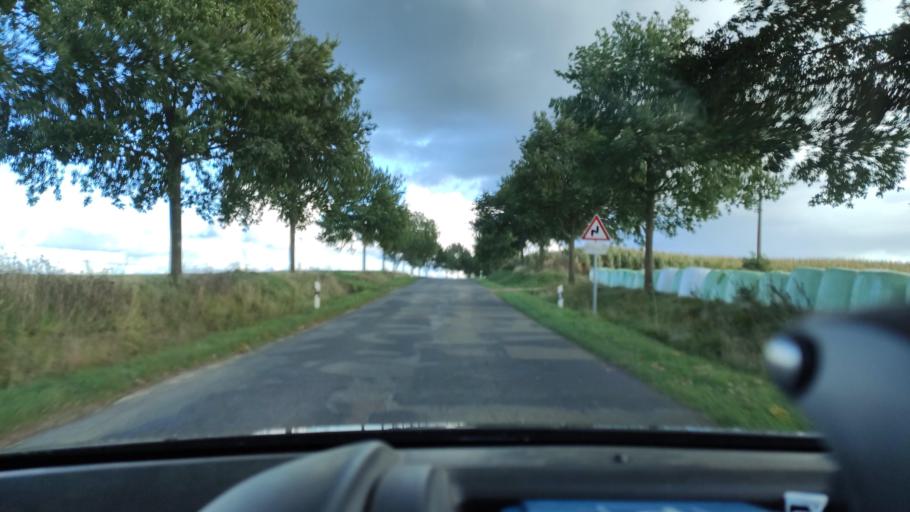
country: DE
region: Mecklenburg-Vorpommern
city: Tarnow
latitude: 53.7972
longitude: 11.9698
